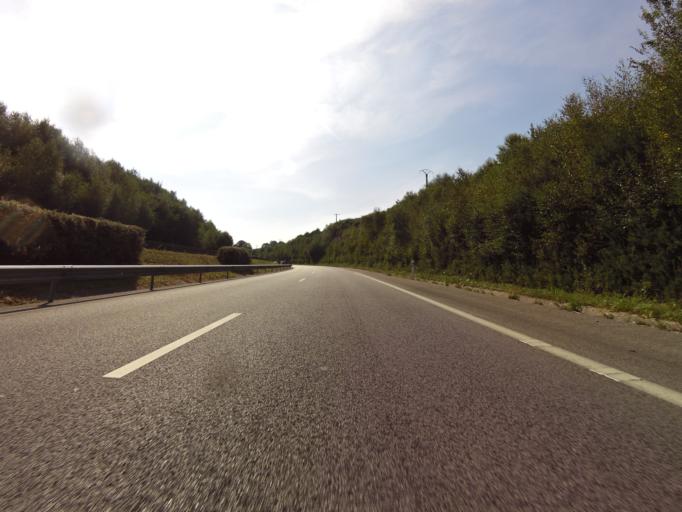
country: FR
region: Brittany
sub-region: Departement du Finistere
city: Quimper
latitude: 48.0030
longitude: -4.1383
